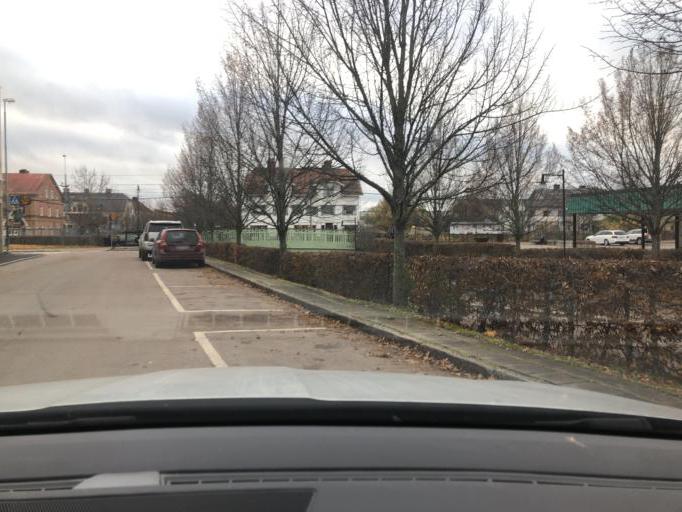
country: SE
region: Uppsala
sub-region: Tierps Kommun
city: Tierp
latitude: 60.3448
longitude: 17.5172
